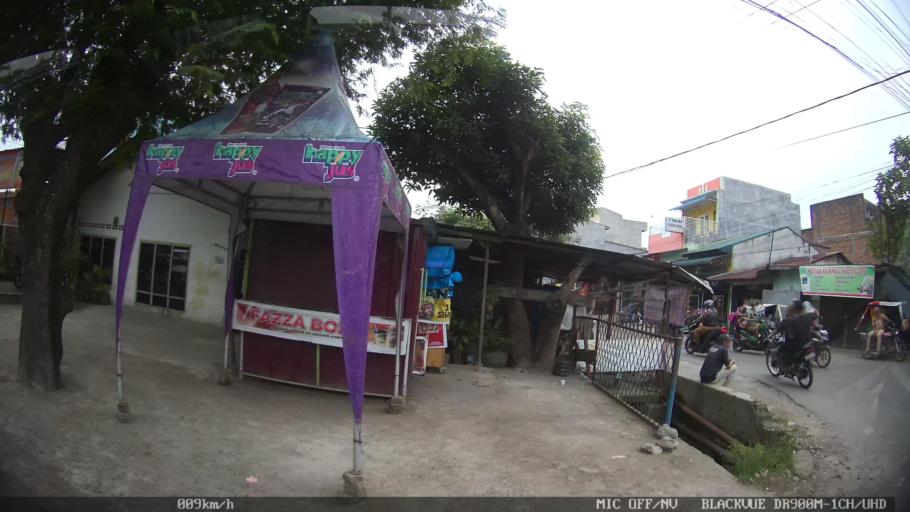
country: ID
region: North Sumatra
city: Deli Tua
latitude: 3.5522
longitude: 98.7118
